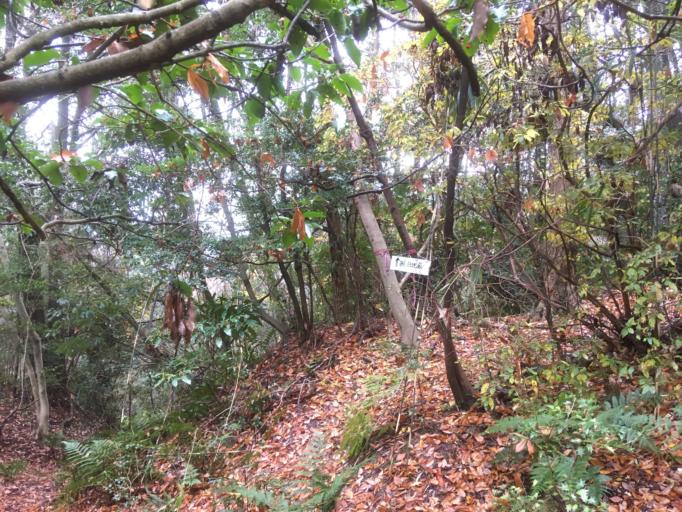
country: JP
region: Nara
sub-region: Ikoma-shi
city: Ikoma
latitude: 34.6932
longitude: 135.6820
